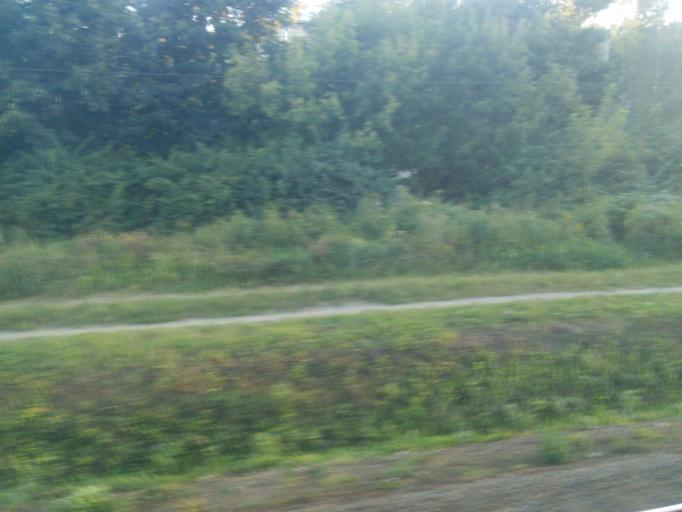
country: RU
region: Moskovskaya
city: Kupavna
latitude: 55.7462
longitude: 38.1464
